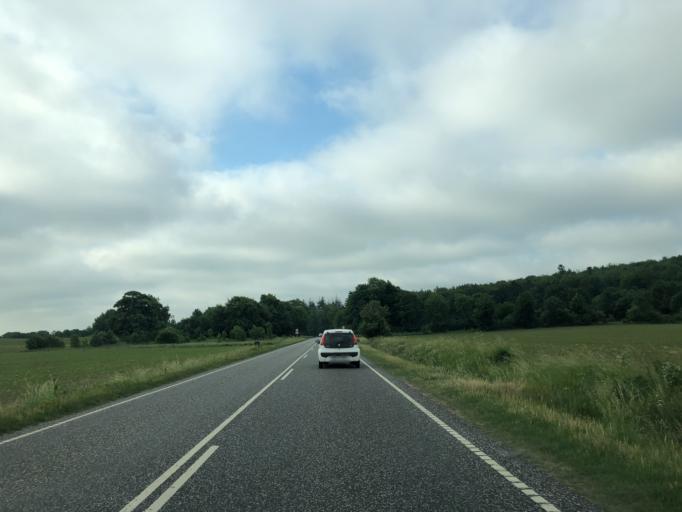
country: DK
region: South Denmark
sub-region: Vejle Kommune
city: Give
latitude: 55.7675
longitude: 9.2905
